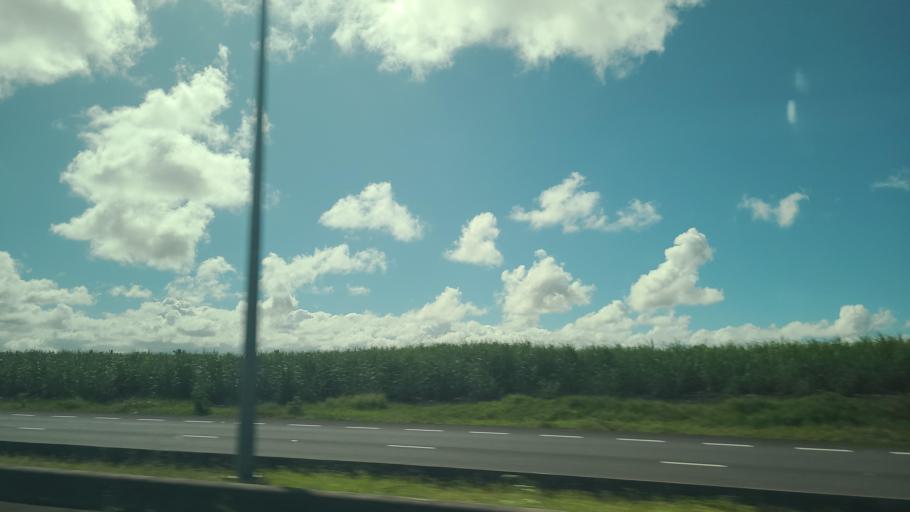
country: MU
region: Grand Port
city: Plaine Magnien
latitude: -20.4388
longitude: 57.6597
